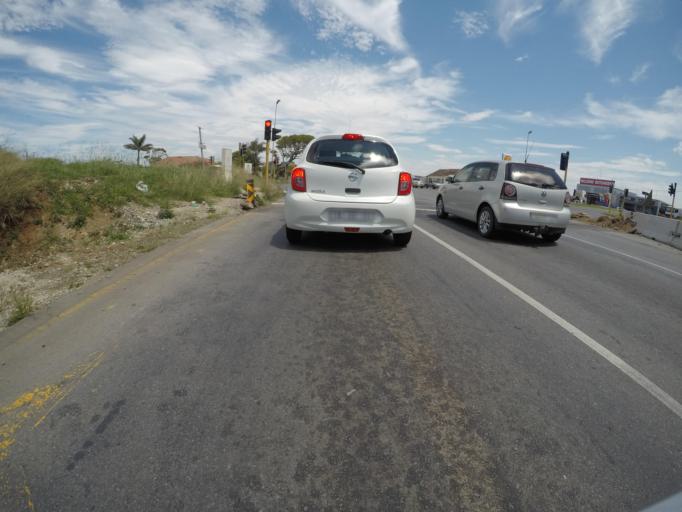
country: ZA
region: Eastern Cape
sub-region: Buffalo City Metropolitan Municipality
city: East London
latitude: -33.0362
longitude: 27.8560
